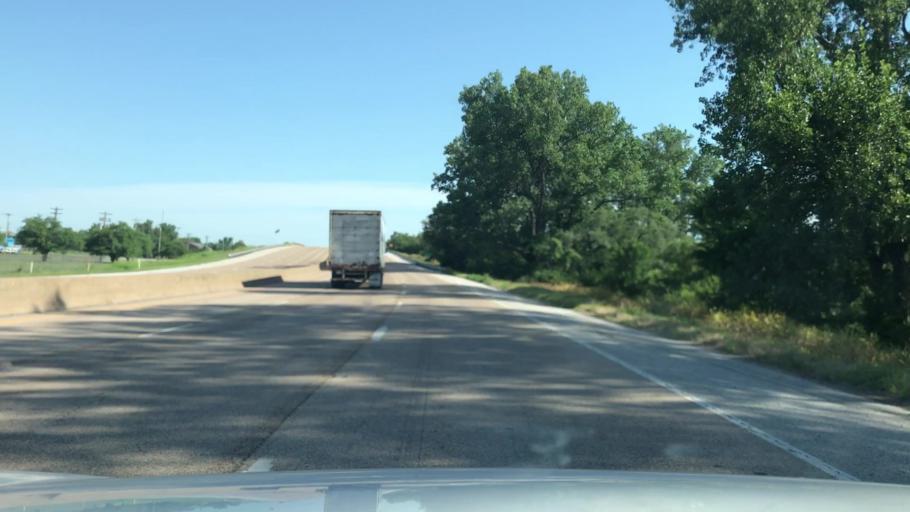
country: US
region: Illinois
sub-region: Madison County
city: Madison
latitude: 38.6950
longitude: -90.1676
